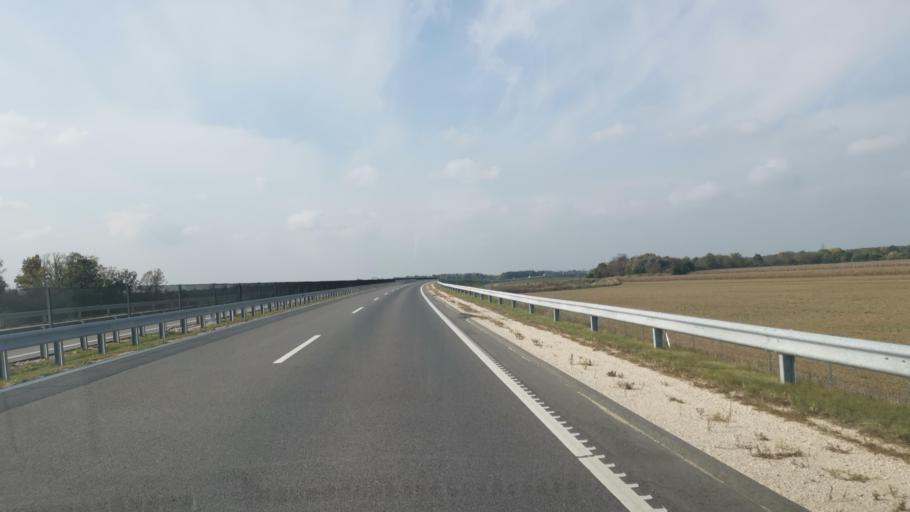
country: HU
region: Gyor-Moson-Sopron
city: Kapuvar
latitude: 47.5704
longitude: 17.0182
